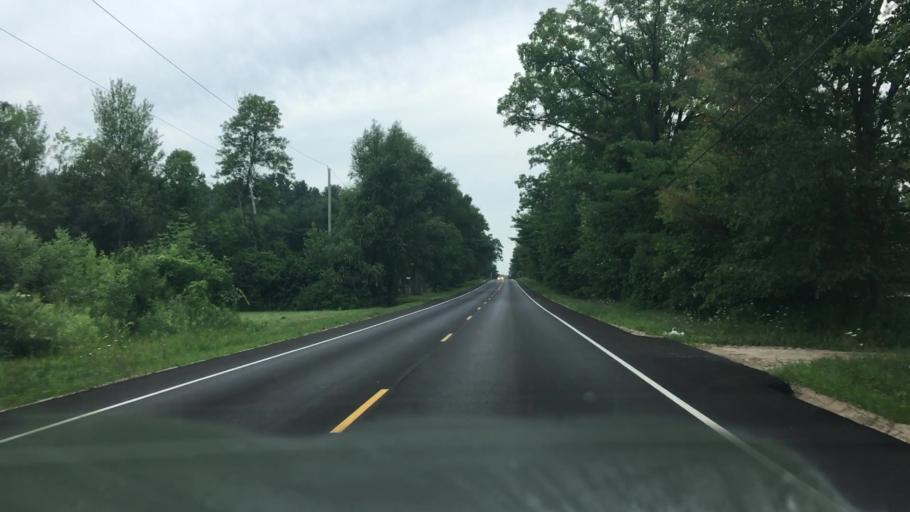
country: US
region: New York
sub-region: Clinton County
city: Morrisonville
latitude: 44.6499
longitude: -73.5494
